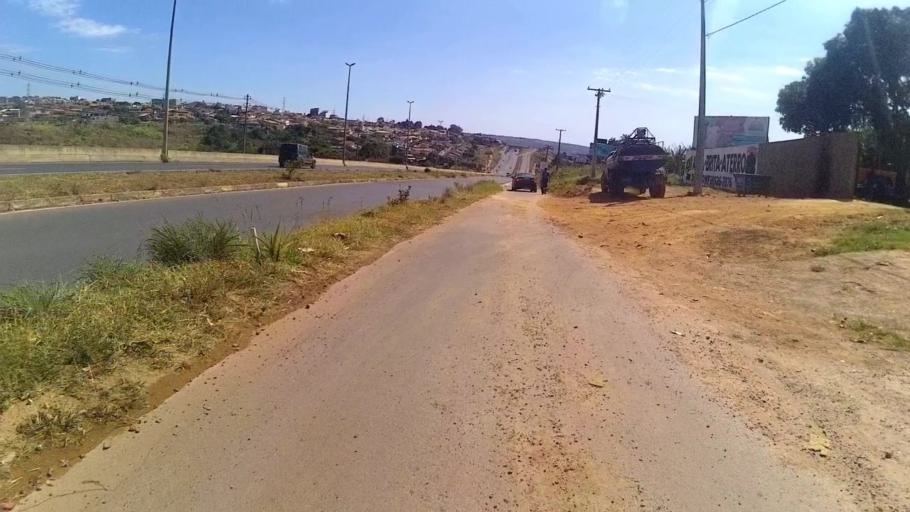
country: BR
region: Federal District
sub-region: Brasilia
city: Brasilia
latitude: -15.6796
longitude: -47.8482
